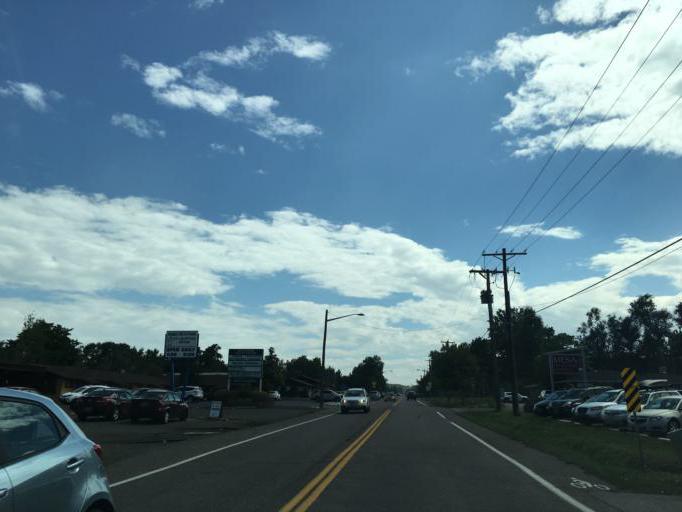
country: US
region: Colorado
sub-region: Jefferson County
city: Applewood
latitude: 39.7536
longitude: -105.1424
